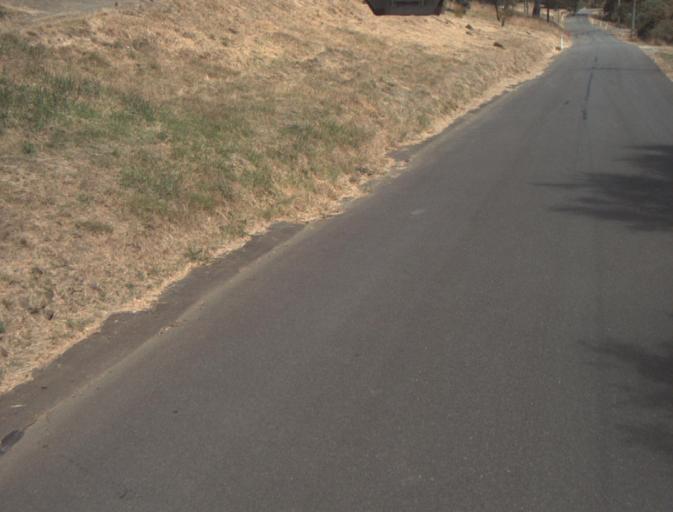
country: AU
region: Tasmania
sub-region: Launceston
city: Summerhill
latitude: -41.4602
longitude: 147.1197
